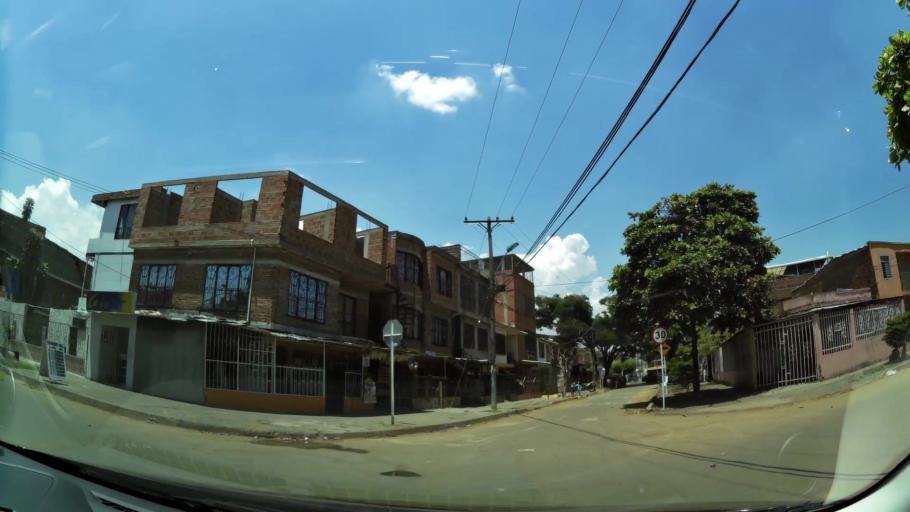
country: CO
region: Valle del Cauca
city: Cali
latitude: 3.4325
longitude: -76.5038
